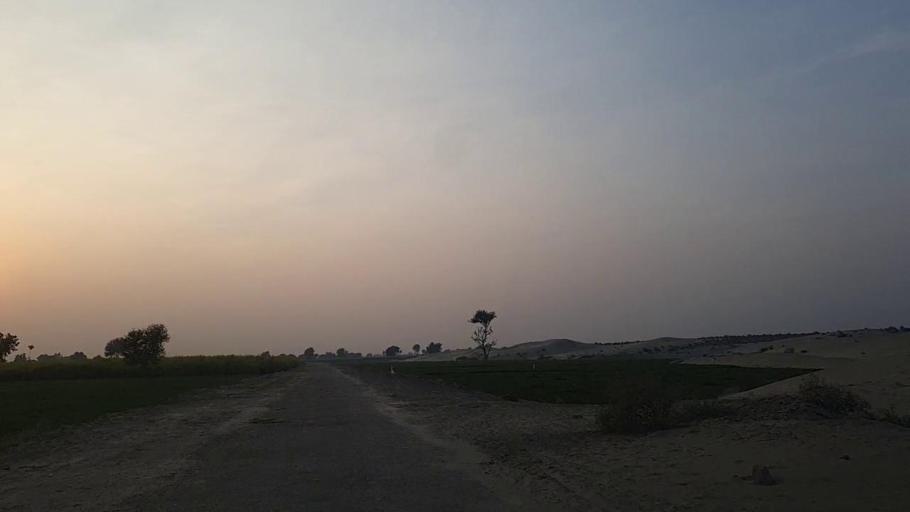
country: PK
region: Sindh
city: Jam Sahib
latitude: 26.4674
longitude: 68.5565
